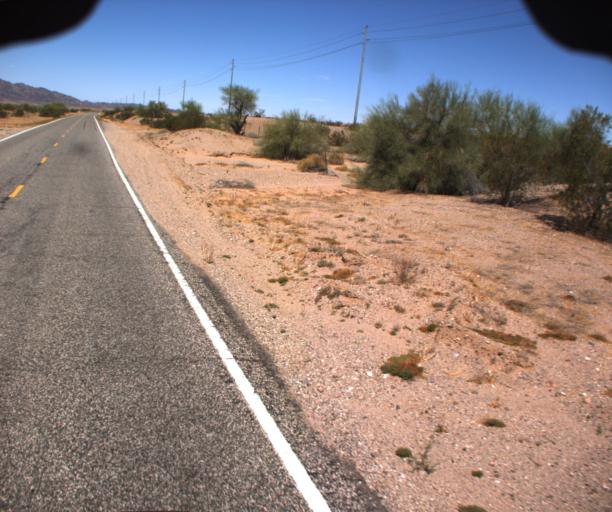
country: US
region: Arizona
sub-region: La Paz County
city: Parker
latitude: 33.9948
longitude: -114.1729
